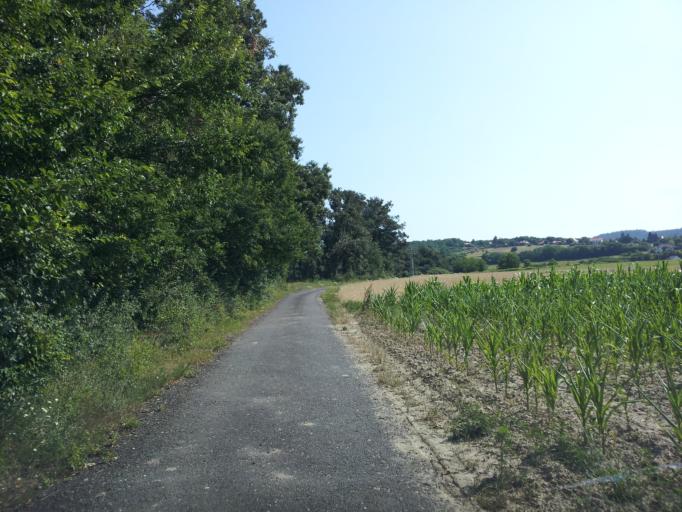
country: HU
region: Zala
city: Cserszegtomaj
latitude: 46.8433
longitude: 17.2085
